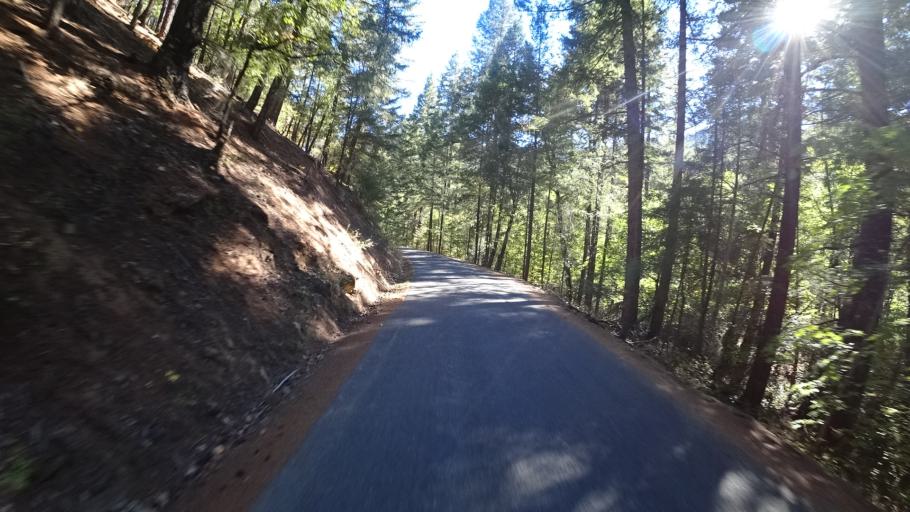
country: US
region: California
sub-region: Siskiyou County
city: Happy Camp
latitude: 41.3103
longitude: -123.1702
